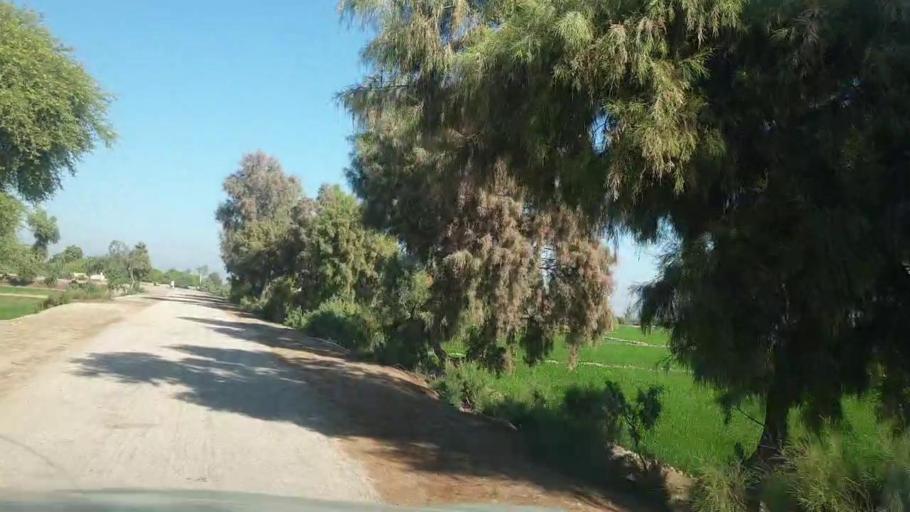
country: PK
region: Sindh
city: Bhan
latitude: 26.5272
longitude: 67.6436
